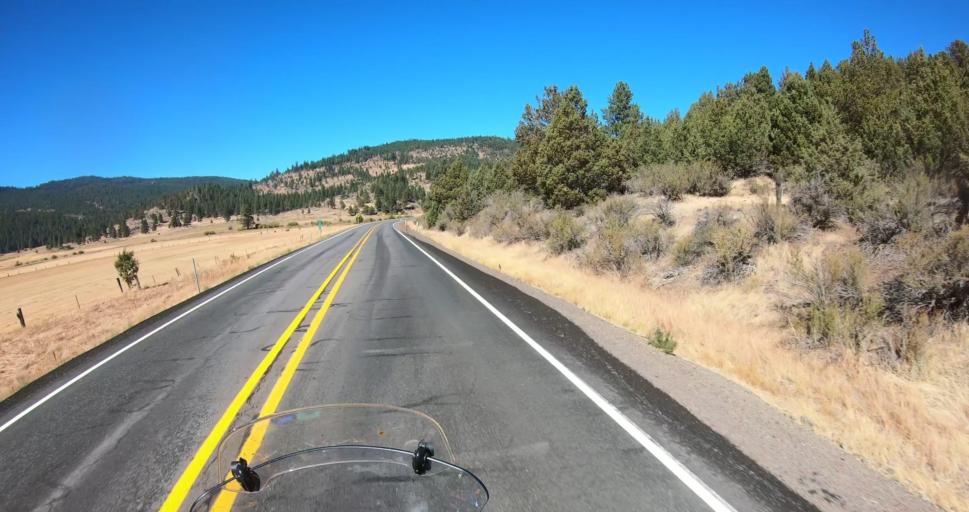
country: US
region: Oregon
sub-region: Lake County
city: Lakeview
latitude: 42.3821
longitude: -120.3047
